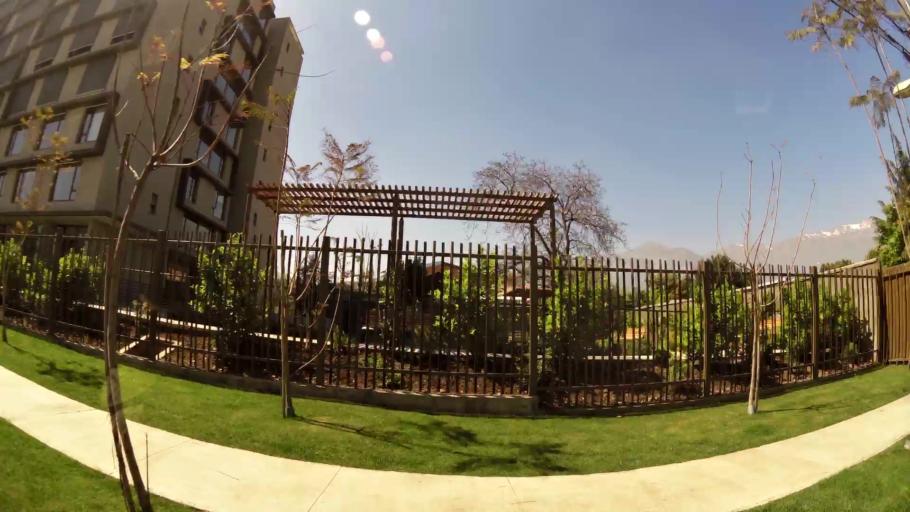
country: CL
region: Santiago Metropolitan
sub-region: Provincia de Santiago
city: Villa Presidente Frei, Nunoa, Santiago, Chile
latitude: -33.4112
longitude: -70.5434
